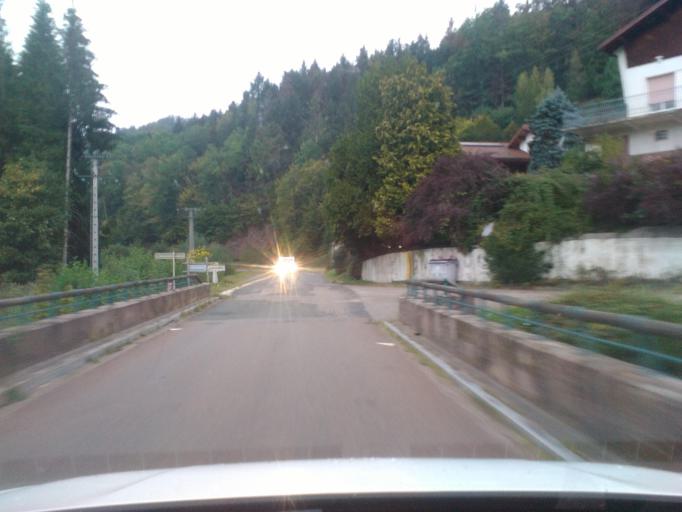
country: FR
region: Lorraine
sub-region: Departement des Vosges
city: Senones
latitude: 48.3381
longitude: 6.9853
